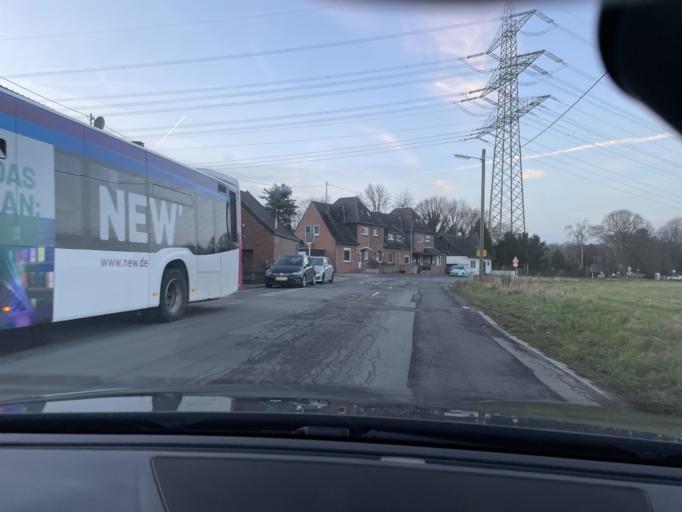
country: DE
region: North Rhine-Westphalia
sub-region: Regierungsbezirk Dusseldorf
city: Monchengladbach
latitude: 51.2317
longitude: 6.4383
